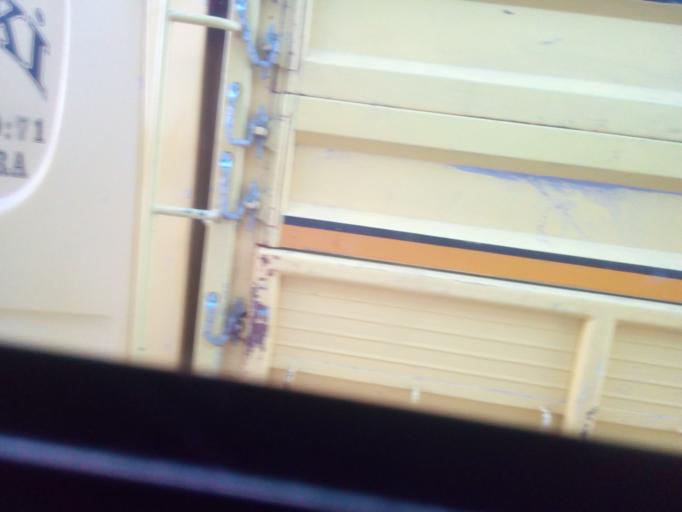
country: TR
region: Ankara
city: Etimesgut
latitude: 39.8888
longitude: 32.6691
